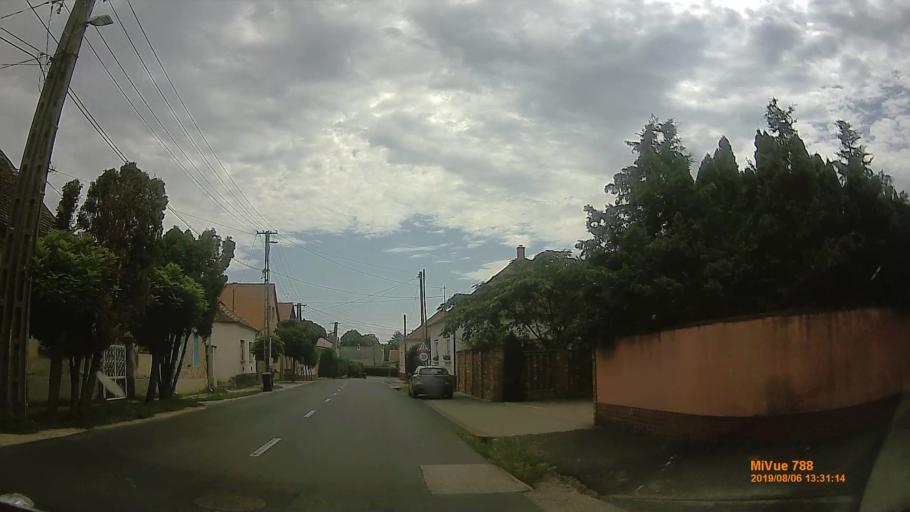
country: HU
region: Vas
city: Gencsapati
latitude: 47.2618
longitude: 16.6017
